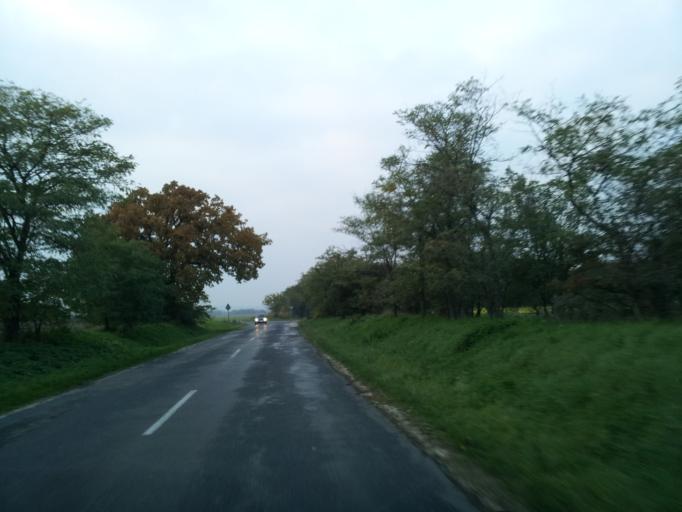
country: HU
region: Gyor-Moson-Sopron
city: Bakonyszentlaszlo
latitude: 47.4689
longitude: 17.8738
